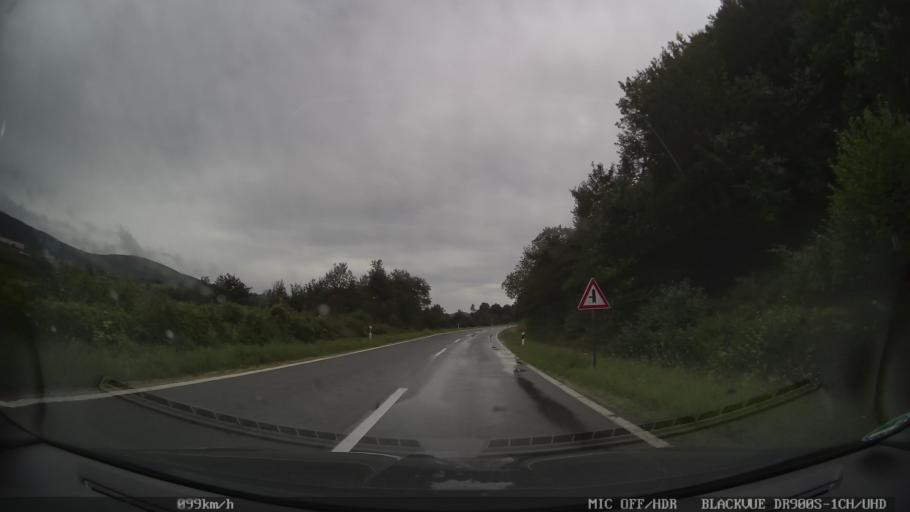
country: HR
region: Licko-Senjska
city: Brinje
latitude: 44.9581
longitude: 15.0954
